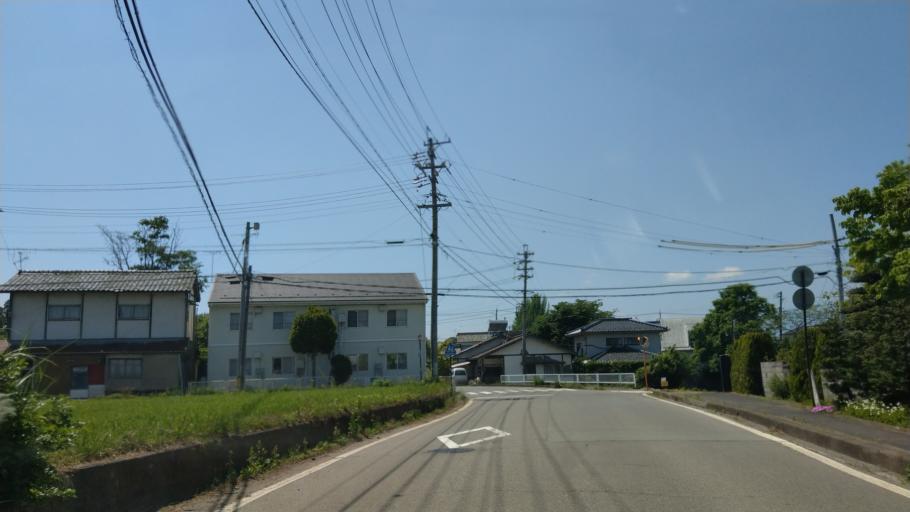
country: JP
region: Nagano
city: Komoro
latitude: 36.2856
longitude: 138.4425
